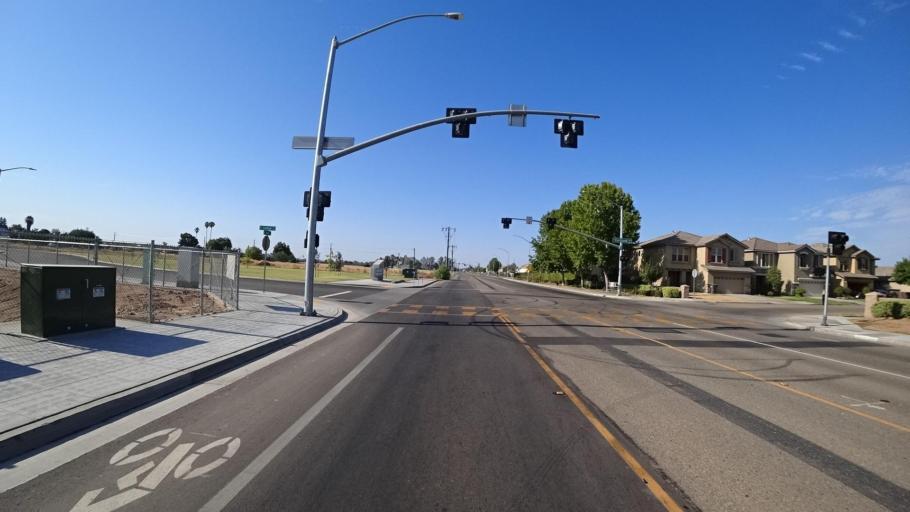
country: US
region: California
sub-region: Fresno County
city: Tarpey Village
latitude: 36.7817
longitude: -119.6550
